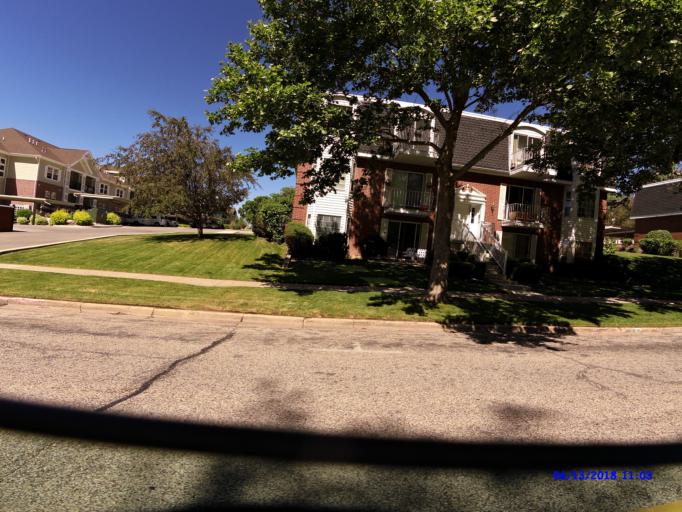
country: US
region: Utah
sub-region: Weber County
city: South Ogden
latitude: 41.2095
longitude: -111.9402
